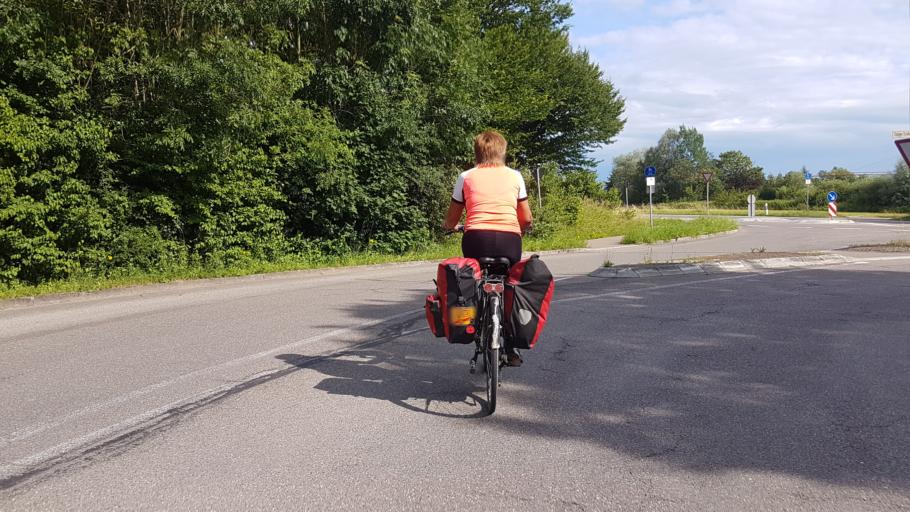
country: DE
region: Baden-Wuerttemberg
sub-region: Tuebingen Region
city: Munderkingen
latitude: 48.2338
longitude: 9.6593
